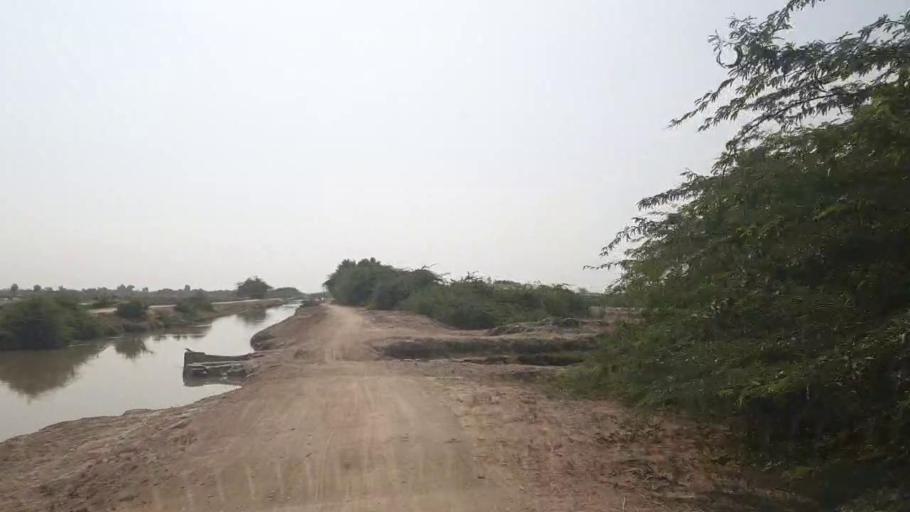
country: PK
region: Sindh
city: Kadhan
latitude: 24.5076
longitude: 68.8502
